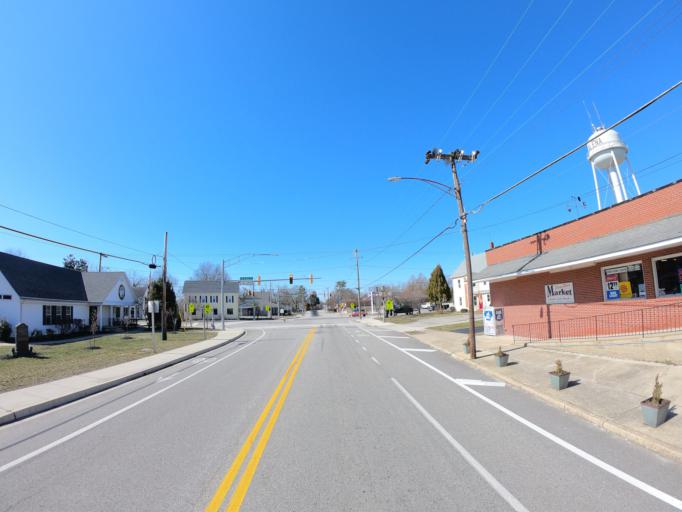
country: US
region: Delaware
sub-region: New Castle County
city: Townsend
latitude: 39.3408
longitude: -75.8779
